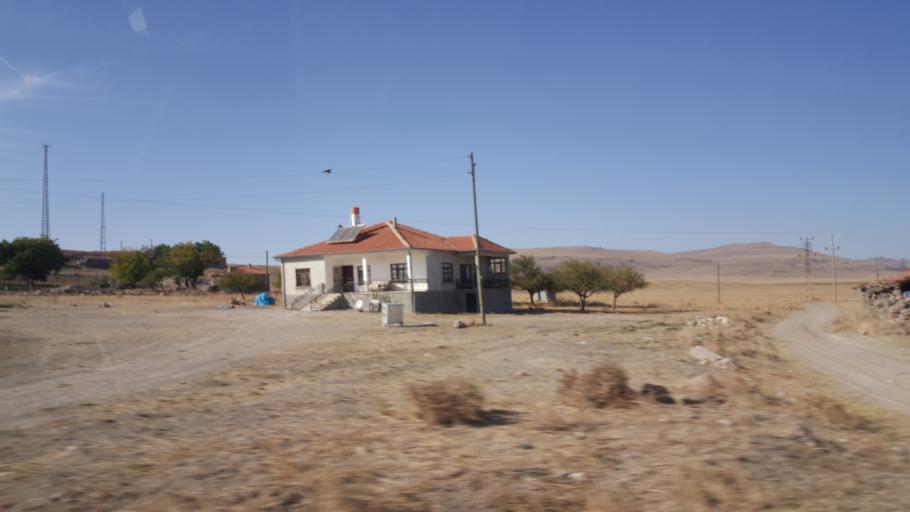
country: TR
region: Ankara
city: Altpinar
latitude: 39.2455
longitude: 32.7475
